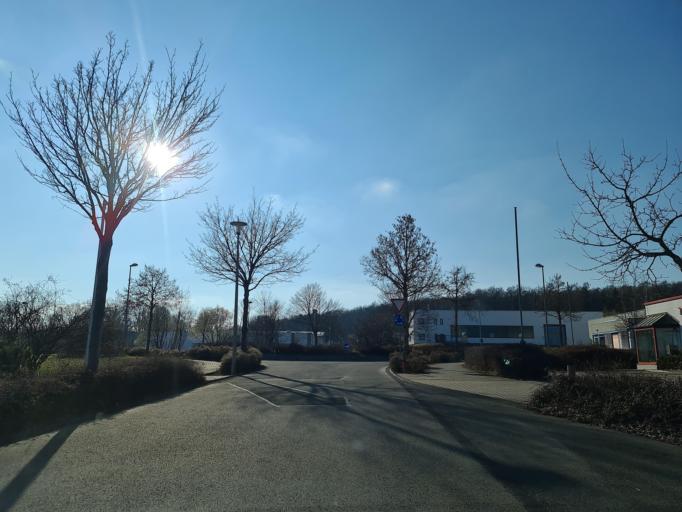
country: DE
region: Saxony
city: Plauen
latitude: 50.5256
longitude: 12.1501
